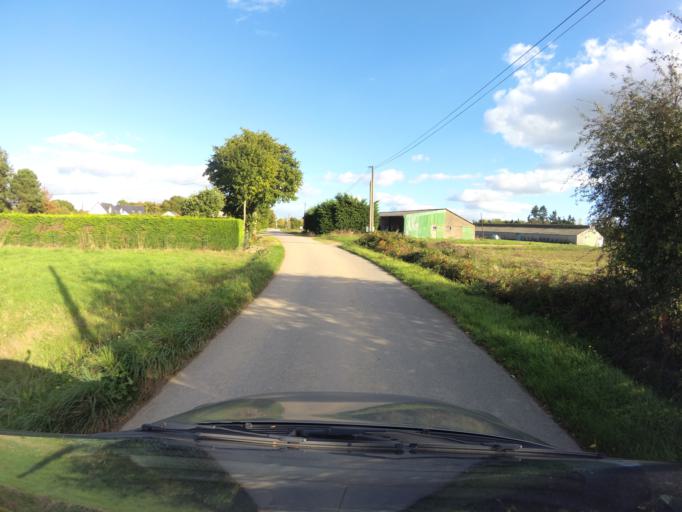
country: FR
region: Brittany
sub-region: Departement du Morbihan
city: Peillac
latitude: 47.7201
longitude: -2.1881
